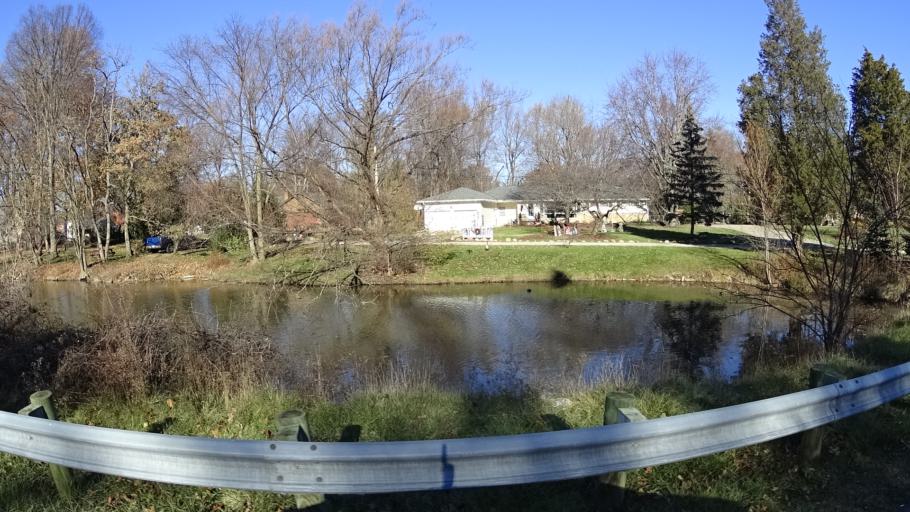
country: US
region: Ohio
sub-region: Lorain County
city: Avon
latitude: 41.4482
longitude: -82.0311
